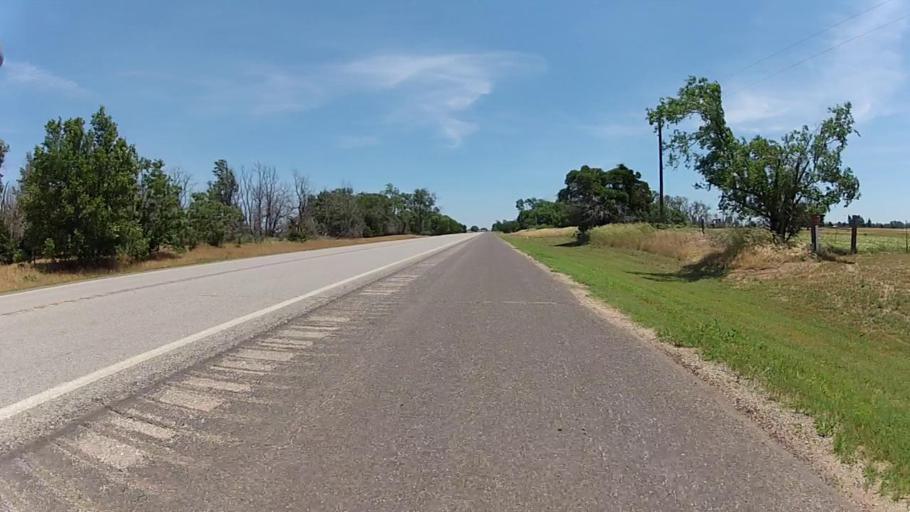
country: US
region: Kansas
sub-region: Barber County
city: Medicine Lodge
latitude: 37.2536
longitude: -98.4073
